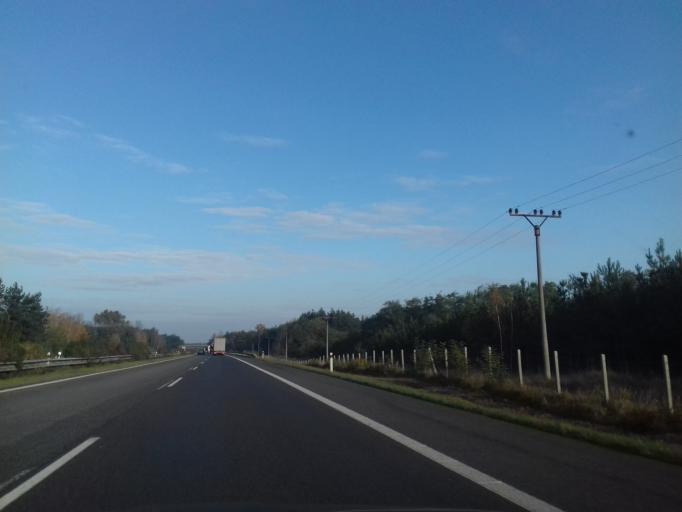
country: SK
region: Bratislavsky
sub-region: Okres Malacky
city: Malacky
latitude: 48.4544
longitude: 17.0404
